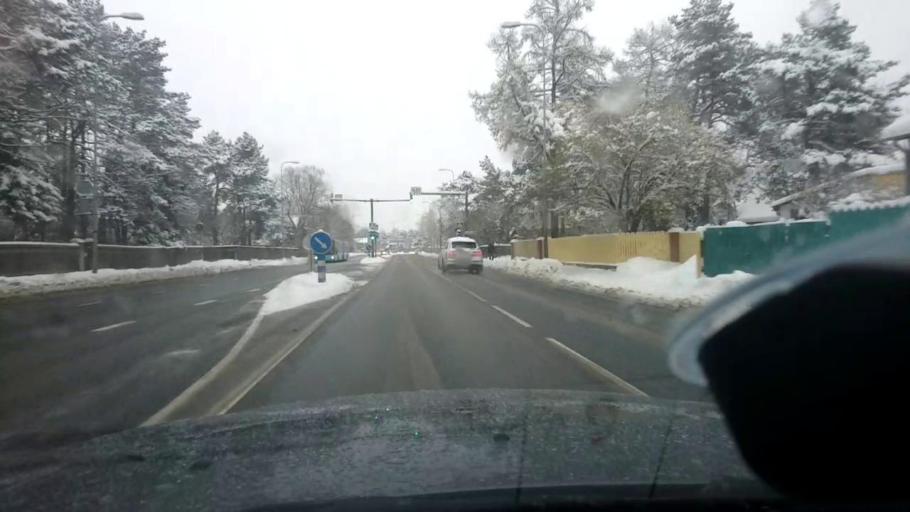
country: EE
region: Harju
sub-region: Tallinna linn
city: Tallinn
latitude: 59.3868
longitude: 24.7149
